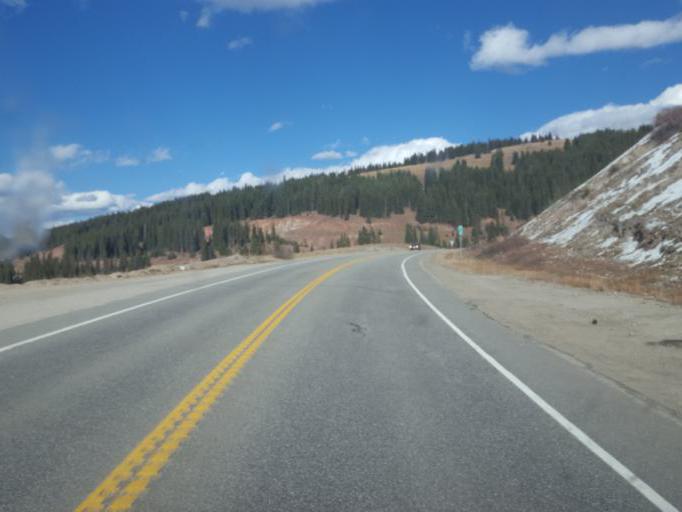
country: US
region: Colorado
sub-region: Lake County
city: Leadville
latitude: 39.3899
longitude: -106.1906
